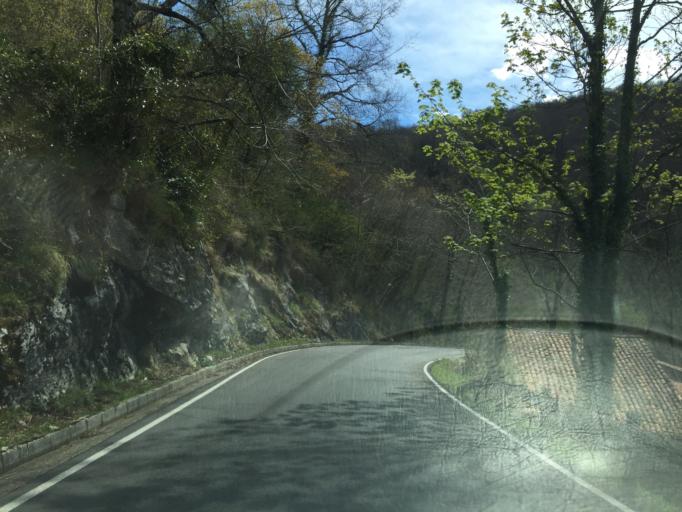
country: ES
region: Asturias
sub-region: Province of Asturias
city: Amieva
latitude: 43.3042
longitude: -5.0433
